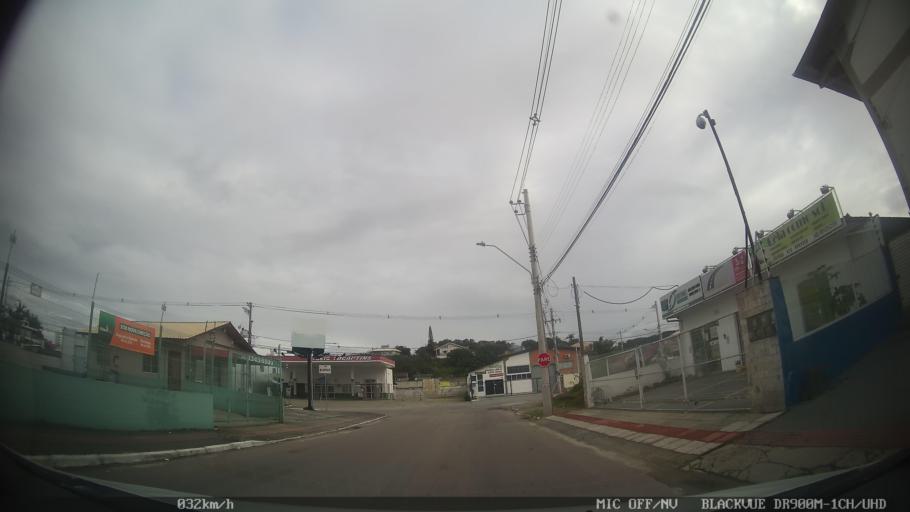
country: BR
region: Santa Catarina
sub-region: Sao Jose
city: Campinas
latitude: -27.5511
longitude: -48.6267
